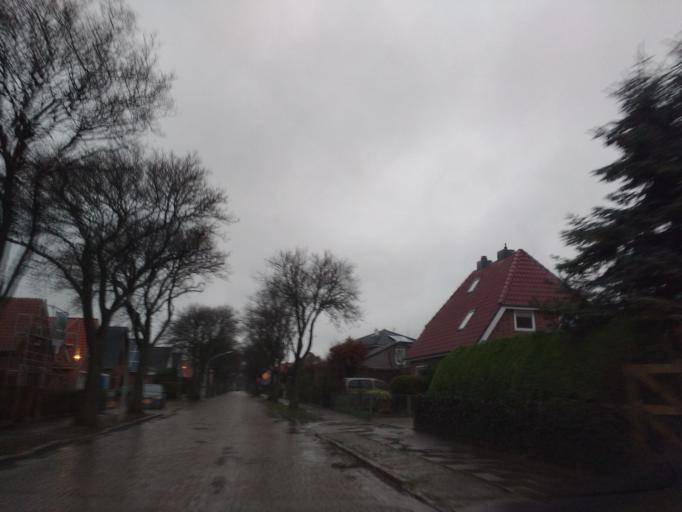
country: DE
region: Schleswig-Holstein
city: Burg auf Fehmarn
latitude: 54.4268
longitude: 11.1929
